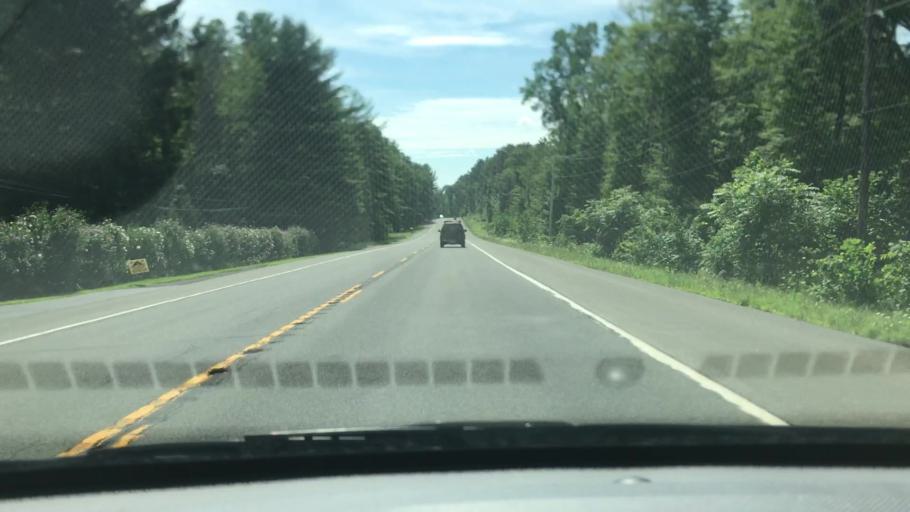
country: US
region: New York
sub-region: Ulster County
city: Shokan
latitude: 41.9817
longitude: -74.2551
